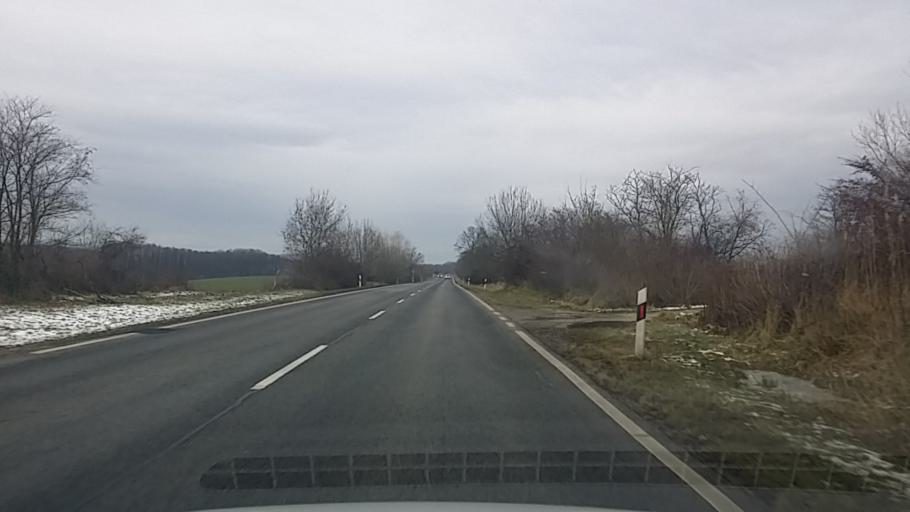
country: HU
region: Komarom-Esztergom
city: Kisber
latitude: 47.4736
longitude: 18.0781
